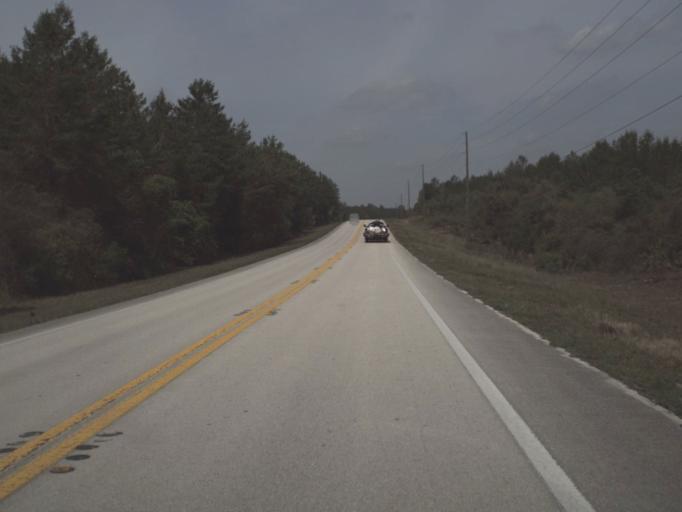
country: US
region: Florida
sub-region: Lake County
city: Astor
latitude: 29.3028
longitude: -81.6755
